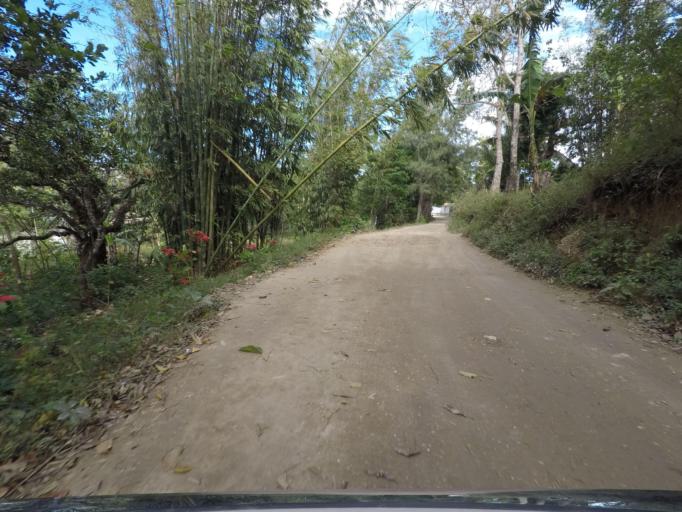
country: TL
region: Baucau
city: Venilale
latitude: -8.6424
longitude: 126.3806
